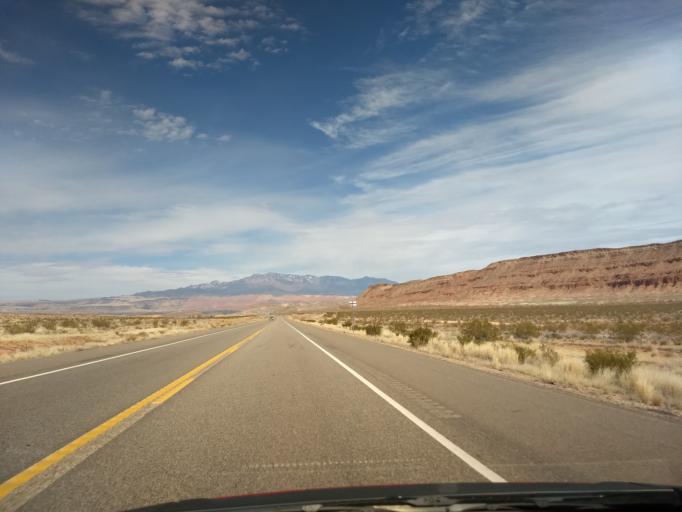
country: US
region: Utah
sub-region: Washington County
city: Washington
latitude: 37.0316
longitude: -113.4848
